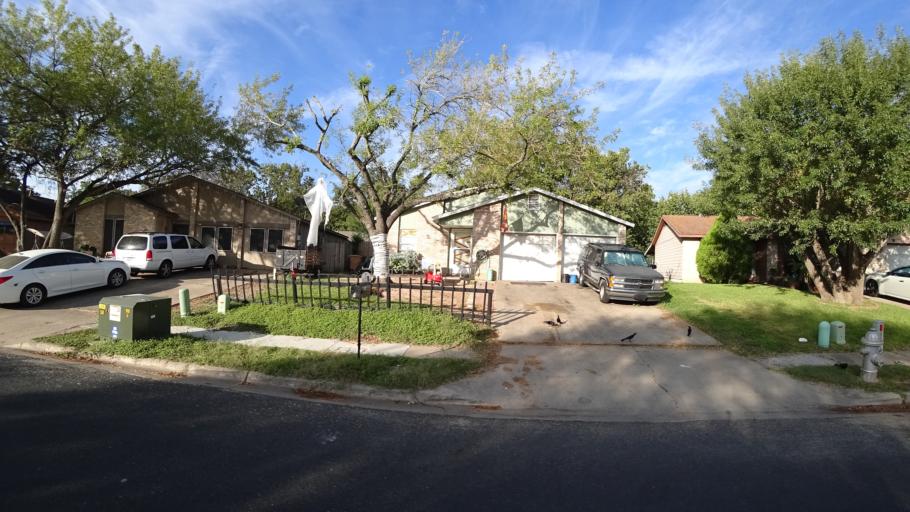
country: US
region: Texas
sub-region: Travis County
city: Onion Creek
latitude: 30.1894
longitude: -97.7489
